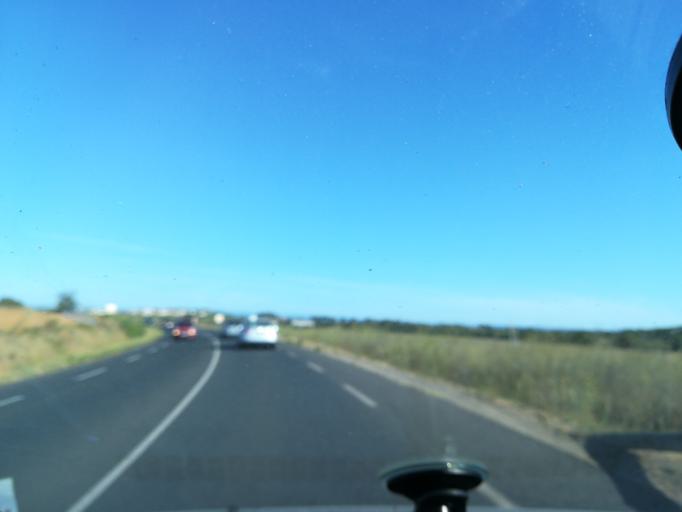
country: FR
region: Languedoc-Roussillon
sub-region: Departement de l'Herault
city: Portiragnes
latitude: 43.2926
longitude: 3.3612
